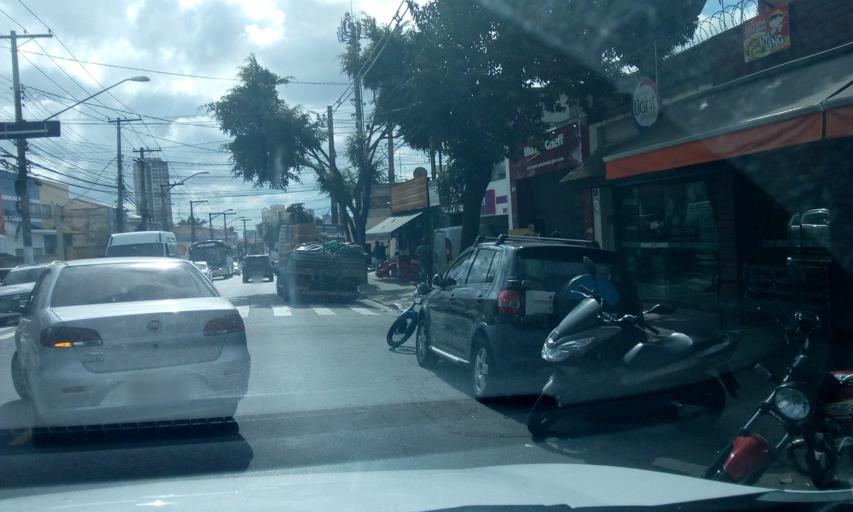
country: BR
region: Sao Paulo
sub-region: Diadema
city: Diadema
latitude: -23.6432
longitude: -46.6656
